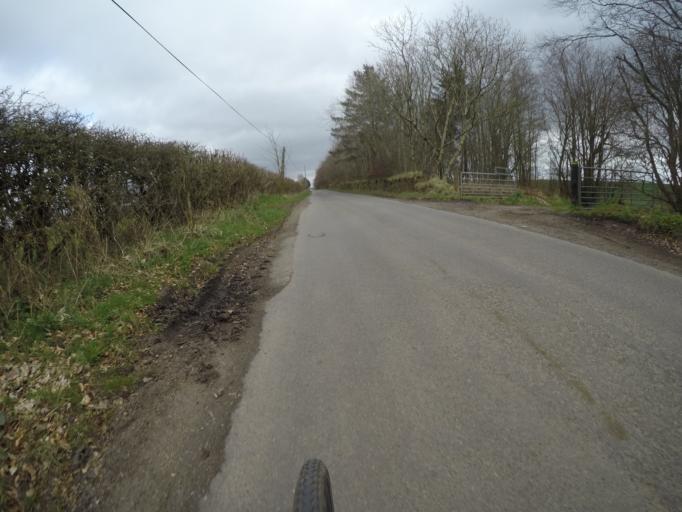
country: GB
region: Scotland
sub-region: East Ayrshire
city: Stewarton
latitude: 55.6763
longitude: -4.5454
